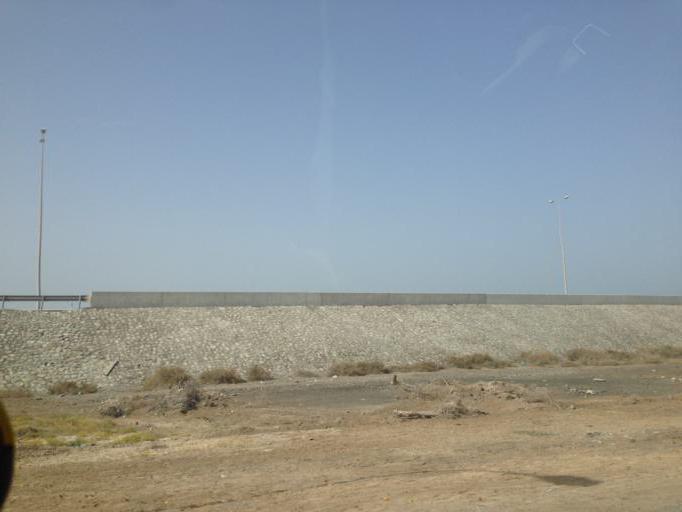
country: OM
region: Al Batinah
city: Barka'
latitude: 23.7068
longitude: 57.9189
